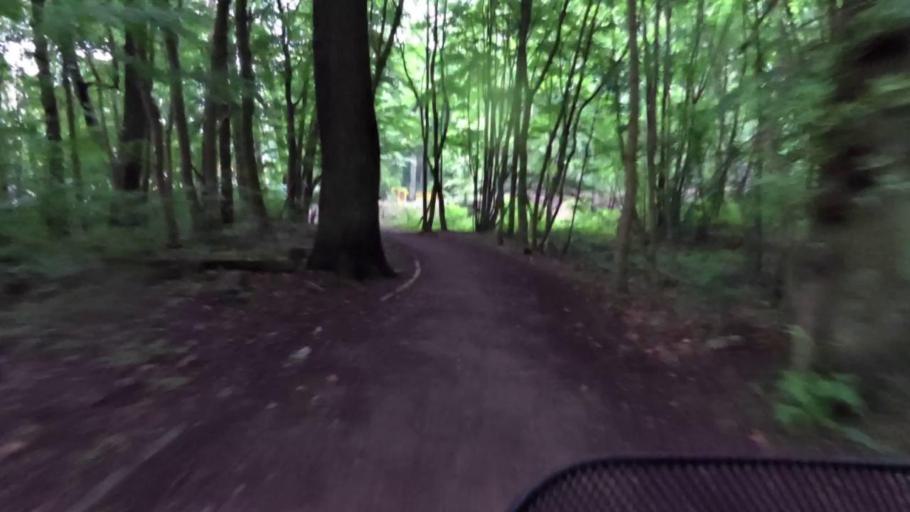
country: PL
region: West Pomeranian Voivodeship
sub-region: Koszalin
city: Koszalin
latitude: 54.1997
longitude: 16.2152
